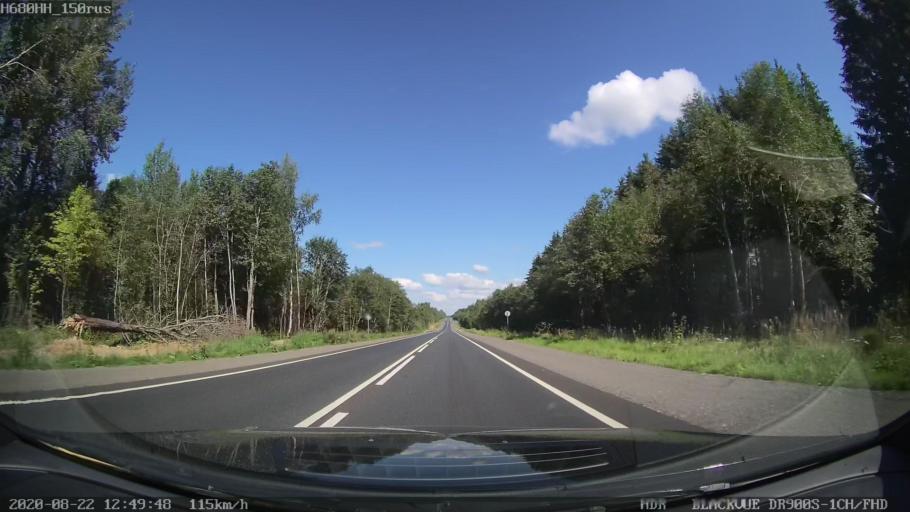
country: RU
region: Tverskaya
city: Rameshki
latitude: 57.4569
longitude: 36.2117
